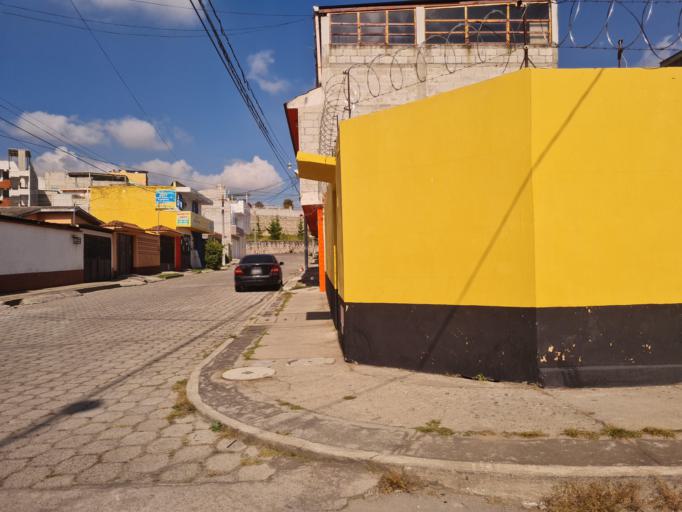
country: GT
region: Quetzaltenango
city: Quetzaltenango
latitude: 14.8401
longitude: -91.5301
